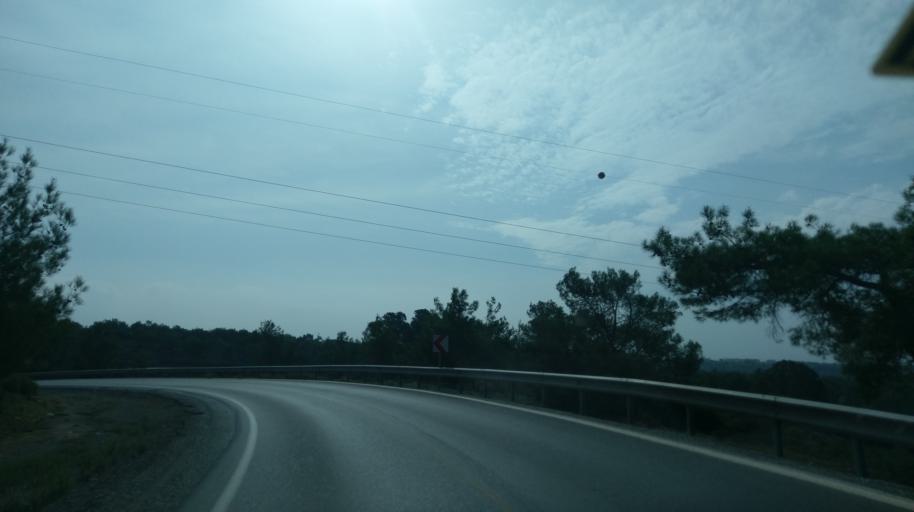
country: CY
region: Lefkosia
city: Morfou
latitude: 35.2678
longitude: 33.0423
